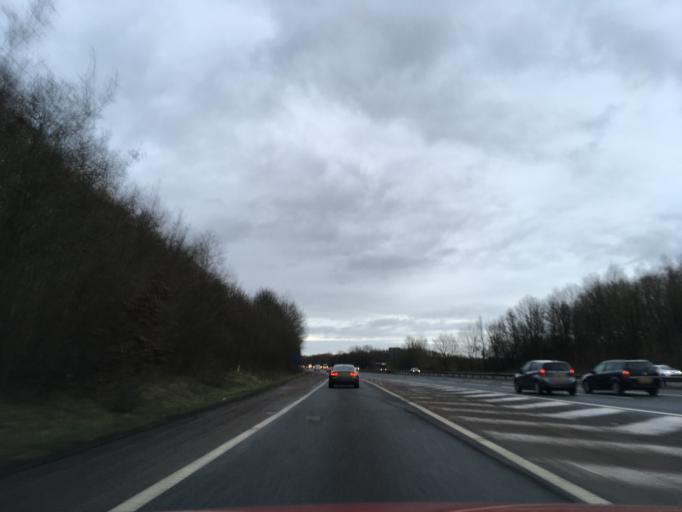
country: GB
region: Wales
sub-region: Rhondda Cynon Taf
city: Llantrisant
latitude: 51.5097
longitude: -3.3532
